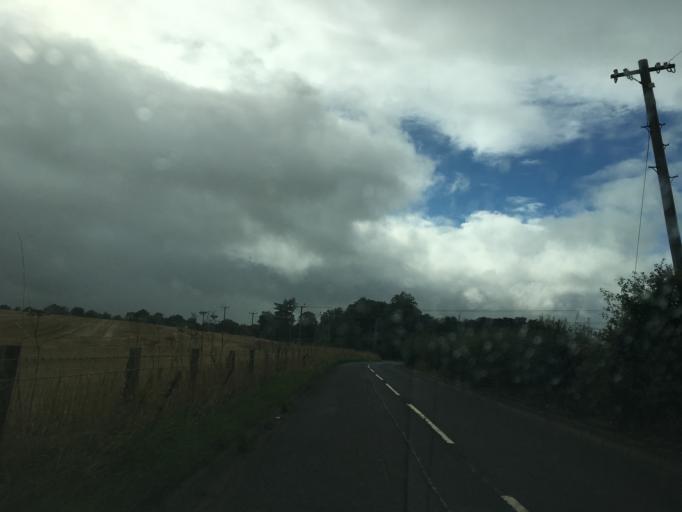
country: GB
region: Scotland
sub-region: Midlothian
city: Loanhead
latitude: 55.8541
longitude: -3.1473
